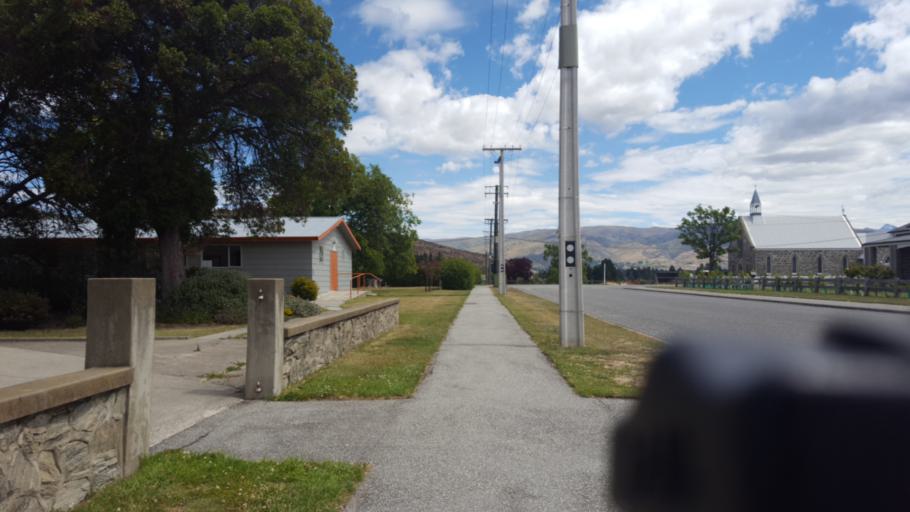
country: NZ
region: Otago
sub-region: Queenstown-Lakes District
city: Wanaka
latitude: -45.0486
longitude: 169.2109
